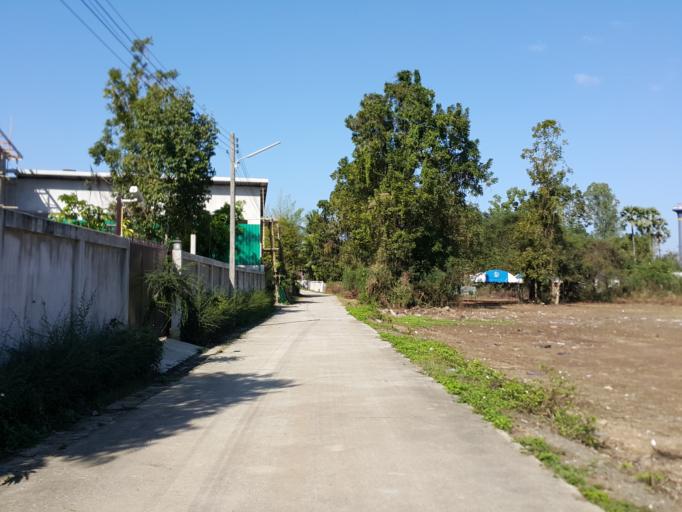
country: TH
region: Chiang Mai
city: San Kamphaeng
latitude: 18.7653
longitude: 99.0896
